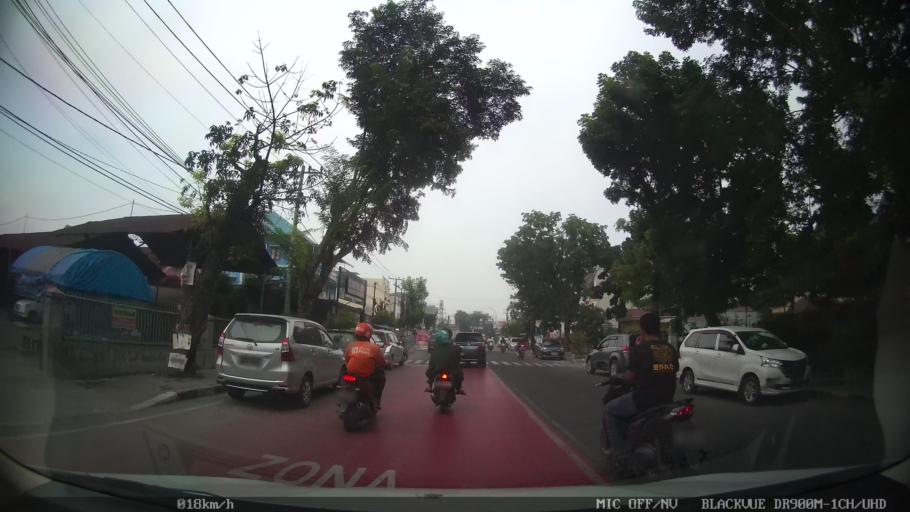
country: ID
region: North Sumatra
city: Medan
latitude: 3.5685
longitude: 98.7017
